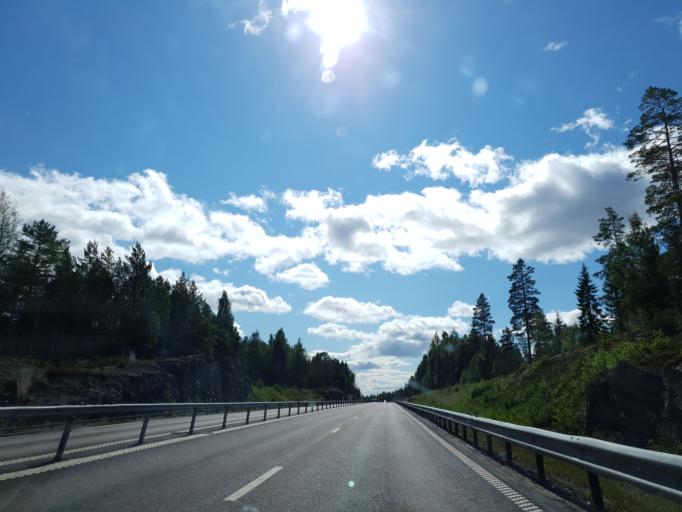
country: SE
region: Vaesternorrland
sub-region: OErnskoeldsviks Kommun
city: Husum
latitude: 63.3851
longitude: 19.1934
